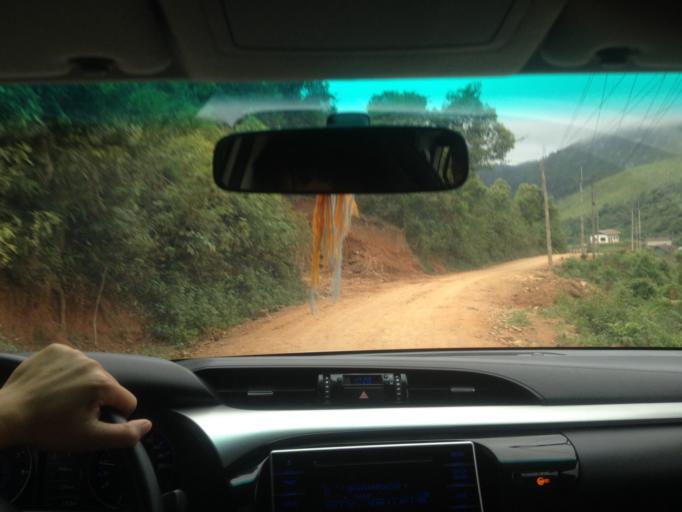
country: TH
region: Nan
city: Chaloem Phra Kiat
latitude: 19.9972
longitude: 101.1293
